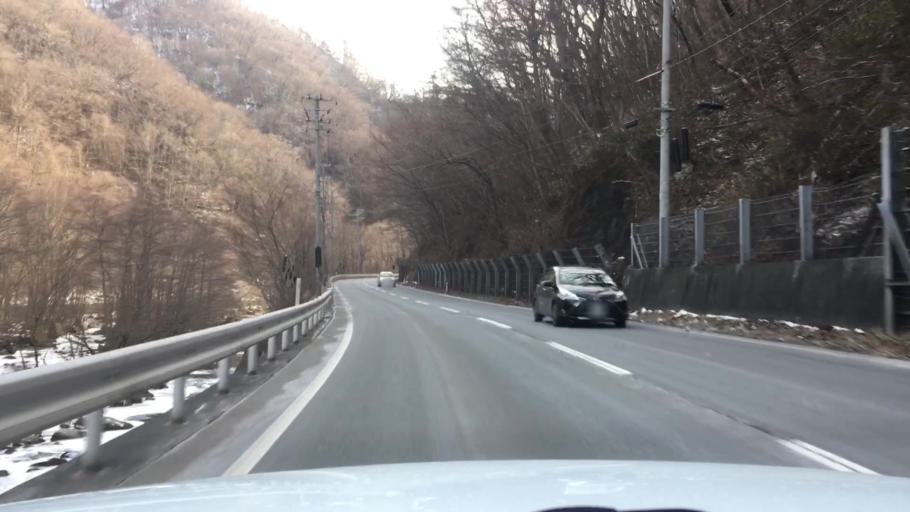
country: JP
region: Iwate
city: Tono
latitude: 39.6376
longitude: 141.5365
